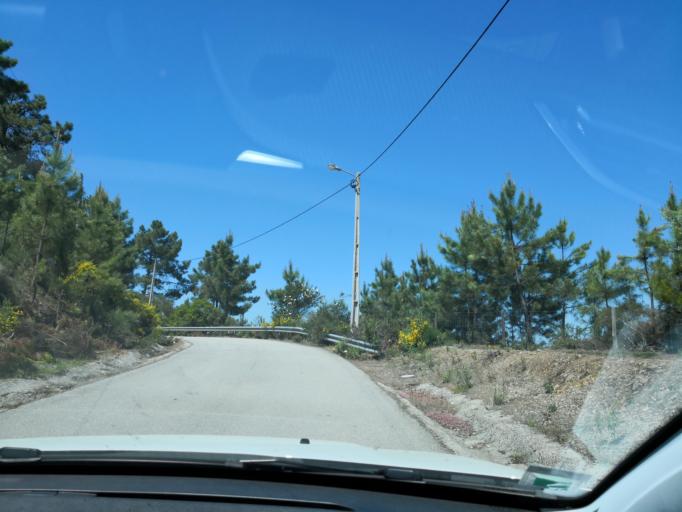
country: PT
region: Vila Real
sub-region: Santa Marta de Penaguiao
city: Santa Marta de Penaguiao
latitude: 41.2164
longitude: -7.7357
